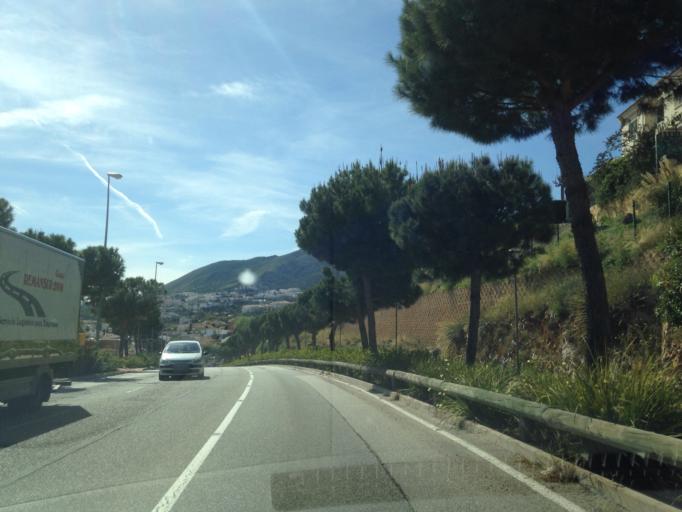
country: ES
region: Andalusia
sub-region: Provincia de Malaga
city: Benalmadena
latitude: 36.6032
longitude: -4.5468
